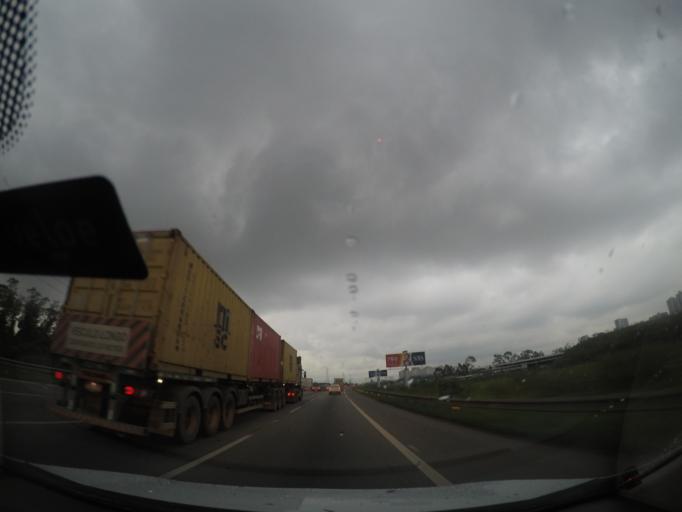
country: BR
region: Sao Paulo
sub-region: Guarulhos
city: Guarulhos
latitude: -23.4873
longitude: -46.5312
